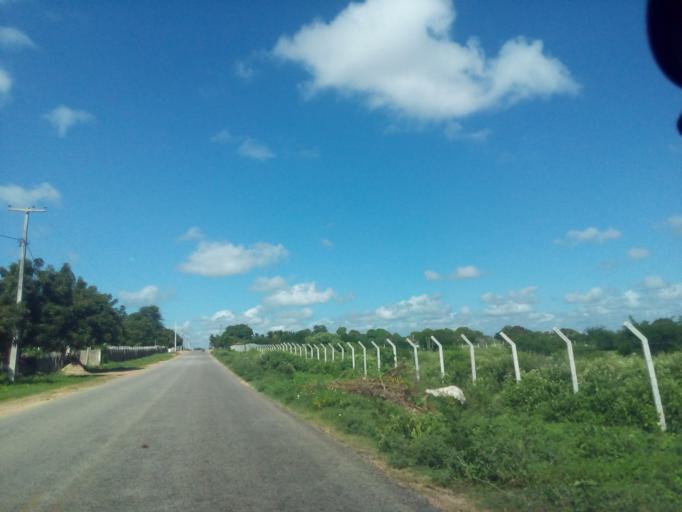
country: BR
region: Rio Grande do Norte
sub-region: Sao Paulo Do Potengi
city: Sao Paulo do Potengi
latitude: -5.9123
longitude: -35.7022
